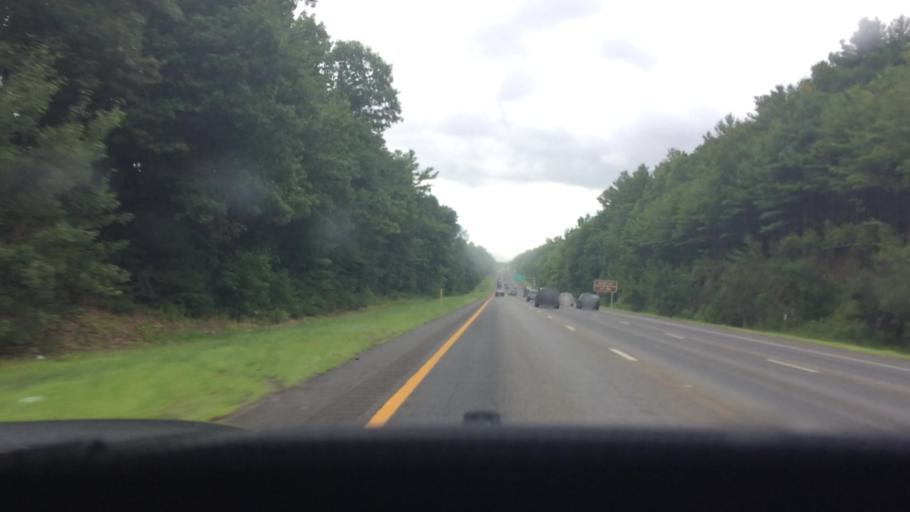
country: US
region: Massachusetts
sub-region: Worcester County
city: Harvard
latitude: 42.5077
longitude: -71.5231
